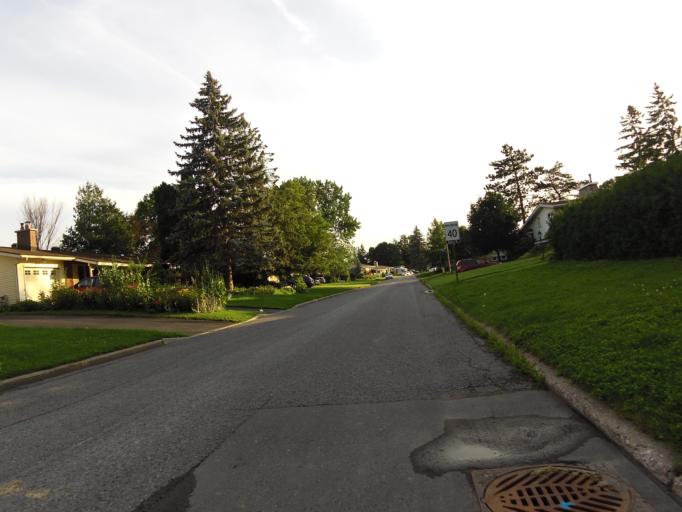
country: CA
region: Ontario
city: Bells Corners
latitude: 45.3470
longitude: -75.8290
